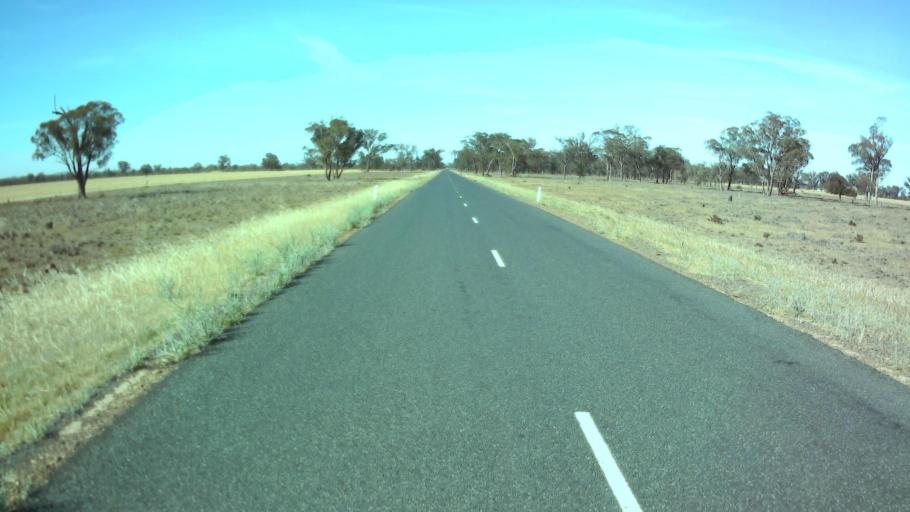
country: AU
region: New South Wales
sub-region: Weddin
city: Grenfell
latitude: -34.0857
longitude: 147.8927
